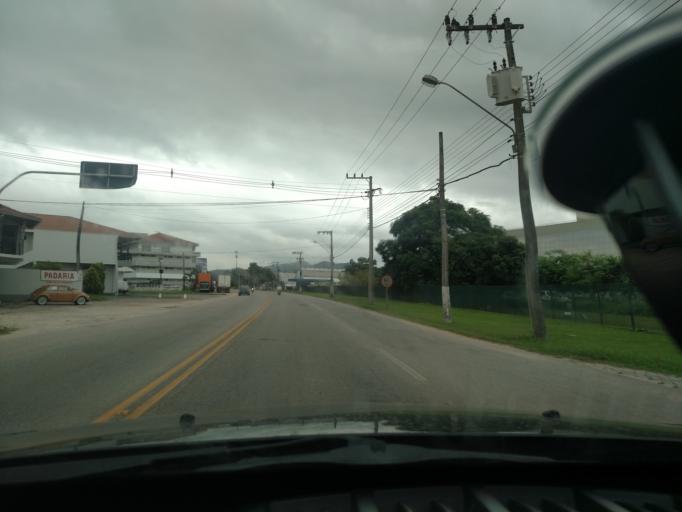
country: BR
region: Santa Catarina
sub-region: Gaspar
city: Gaspar
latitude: -26.9151
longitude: -48.9081
